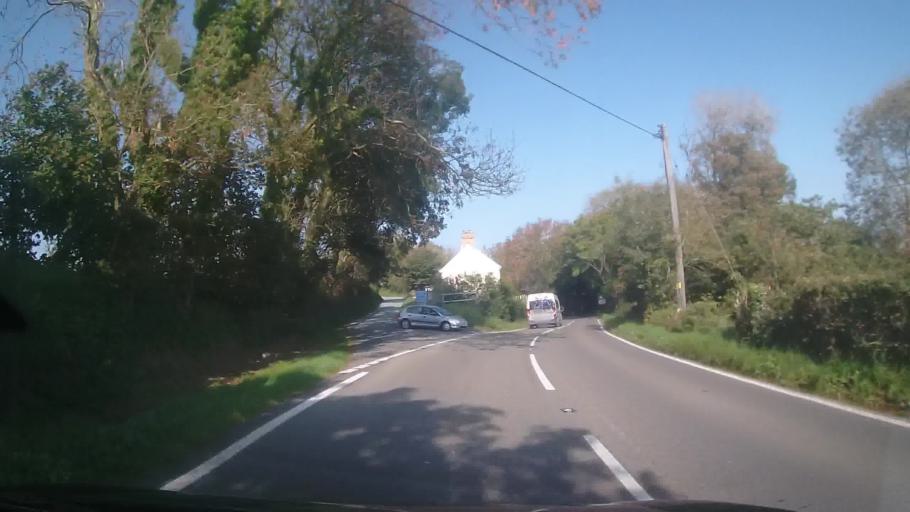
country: GB
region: Wales
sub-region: County of Ceredigion
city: Cardigan
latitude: 52.0643
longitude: -4.6817
